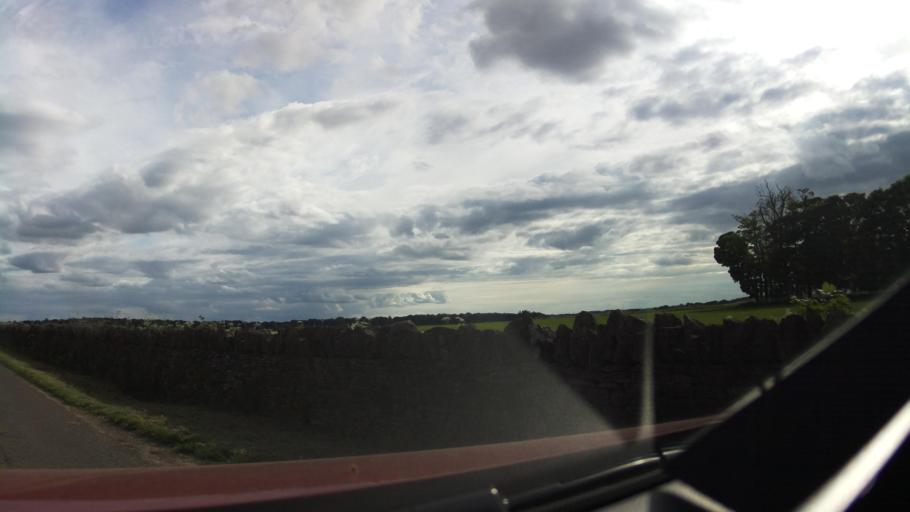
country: GB
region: England
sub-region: Gloucestershire
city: Westfield
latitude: 51.8899
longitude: -1.8881
